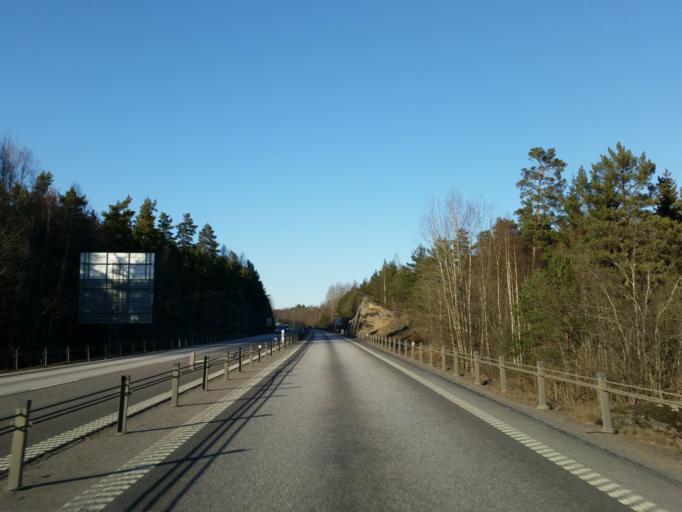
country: SE
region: Kalmar
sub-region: Oskarshamns Kommun
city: Oskarshamn
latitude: 57.2805
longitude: 16.4498
